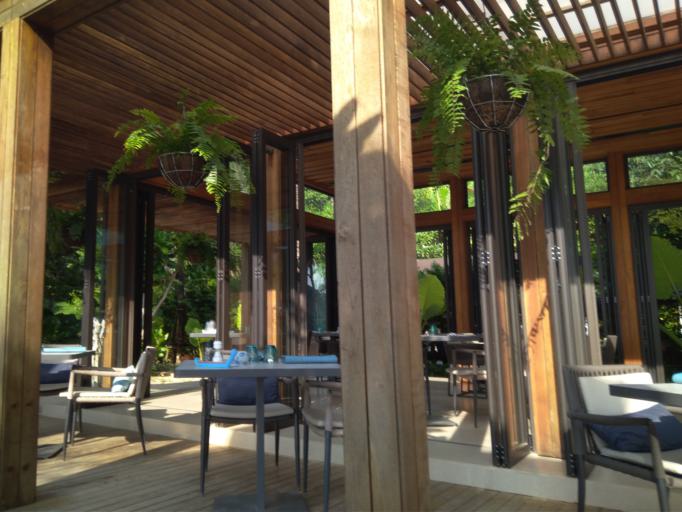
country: TH
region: Krabi
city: Ko Lanta
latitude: 7.4951
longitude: 99.0751
